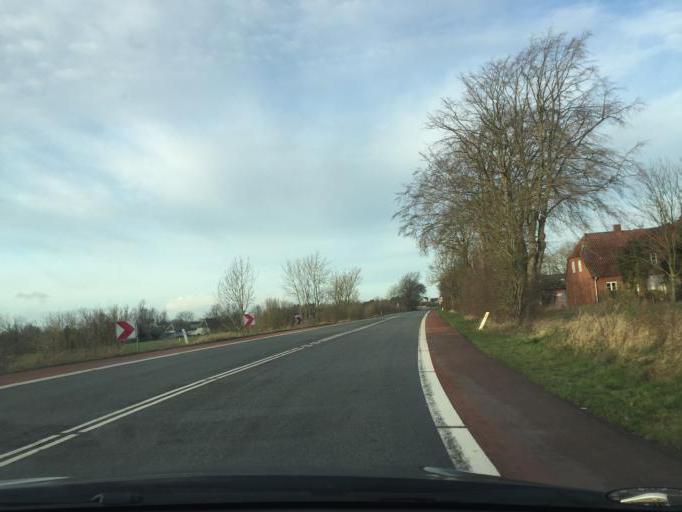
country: DK
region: South Denmark
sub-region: Faaborg-Midtfyn Kommune
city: Ringe
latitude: 55.2694
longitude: 10.4520
